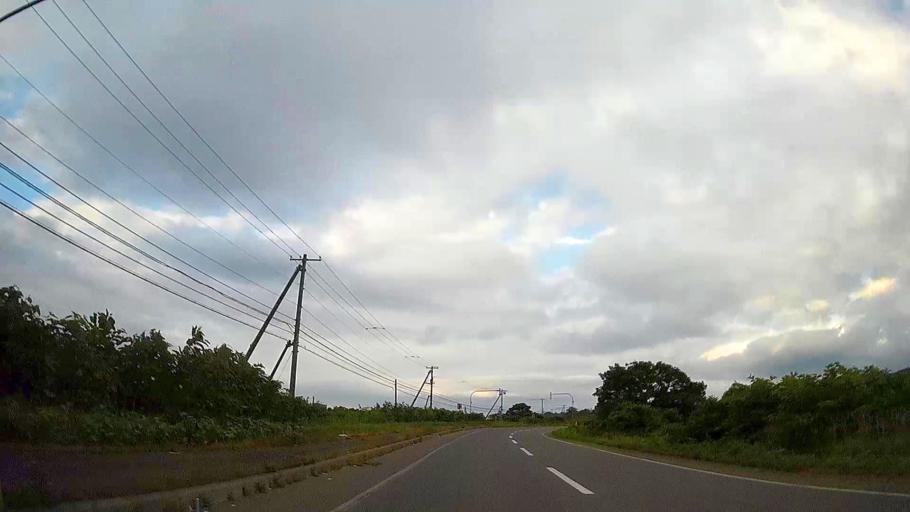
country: JP
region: Hokkaido
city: Nanae
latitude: 42.1280
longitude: 140.7123
